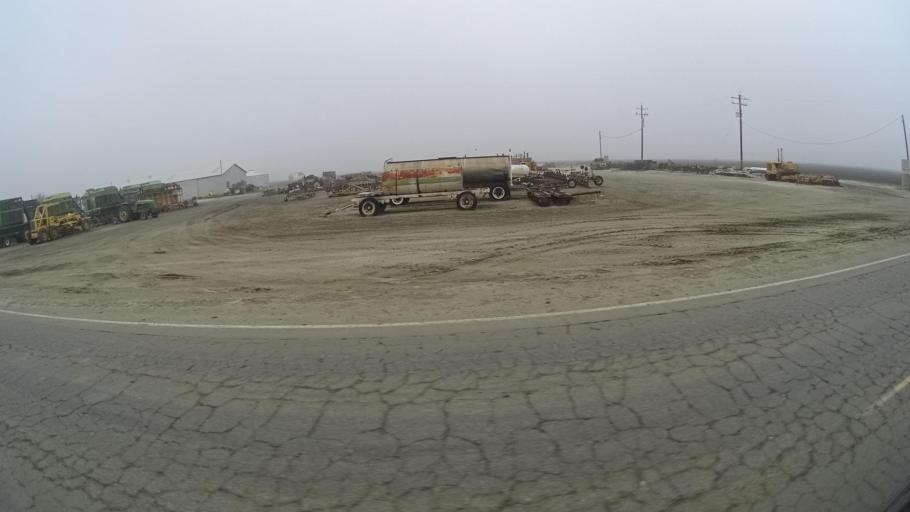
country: US
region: California
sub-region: Kern County
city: Buttonwillow
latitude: 35.4384
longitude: -119.5180
